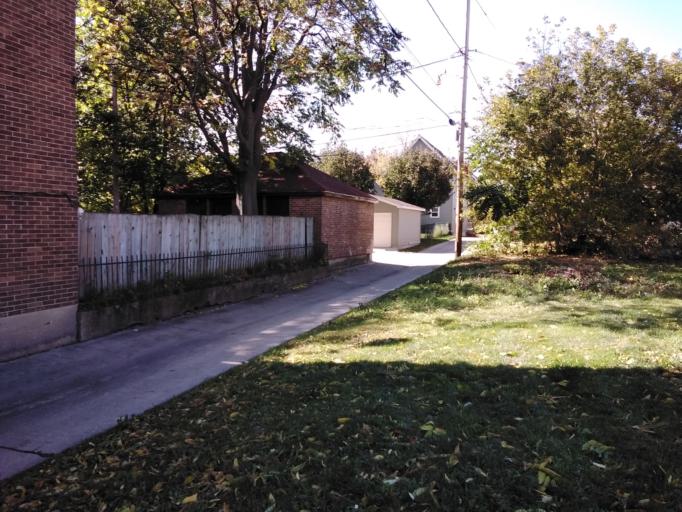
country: US
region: Wisconsin
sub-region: Milwaukee County
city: Milwaukee
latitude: 43.0639
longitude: -87.9490
